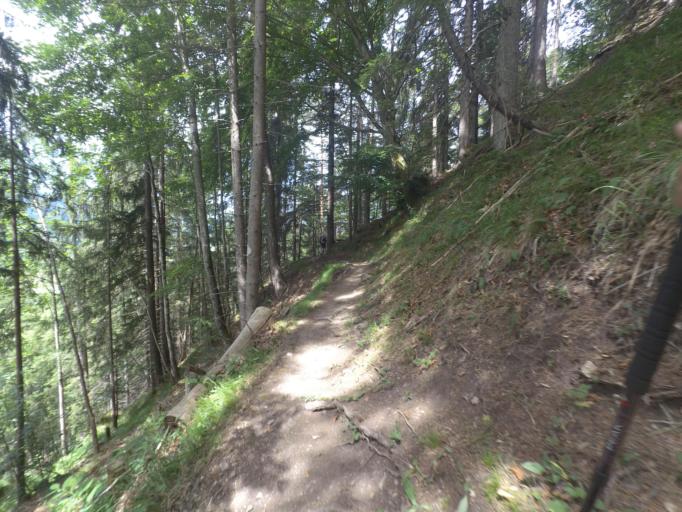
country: AT
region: Salzburg
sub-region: Politischer Bezirk Zell am See
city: Saalfelden am Steinernen Meer
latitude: 47.4441
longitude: 12.8576
